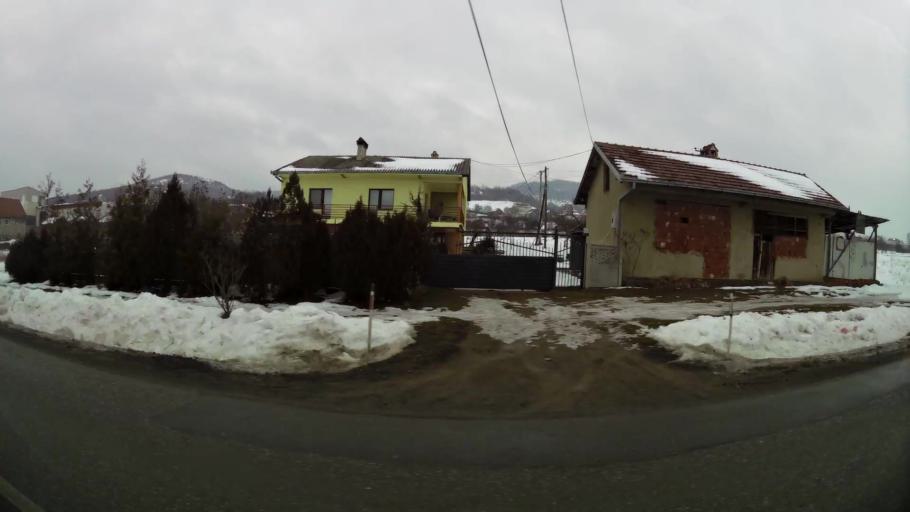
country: XK
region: Pristina
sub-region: Komuna e Prishtines
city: Pristina
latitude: 42.7214
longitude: 21.1468
